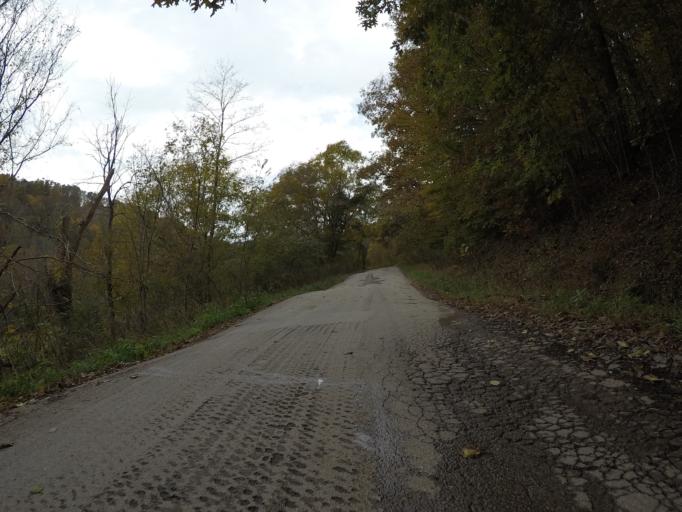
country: US
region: West Virginia
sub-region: Wayne County
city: Lavalette
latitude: 38.3449
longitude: -82.4298
